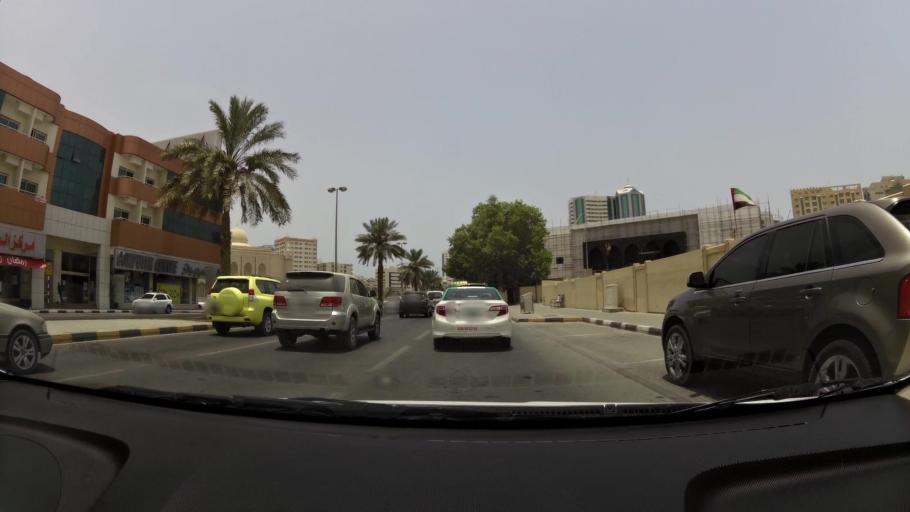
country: AE
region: Ash Shariqah
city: Sharjah
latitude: 25.3512
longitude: 55.3932
